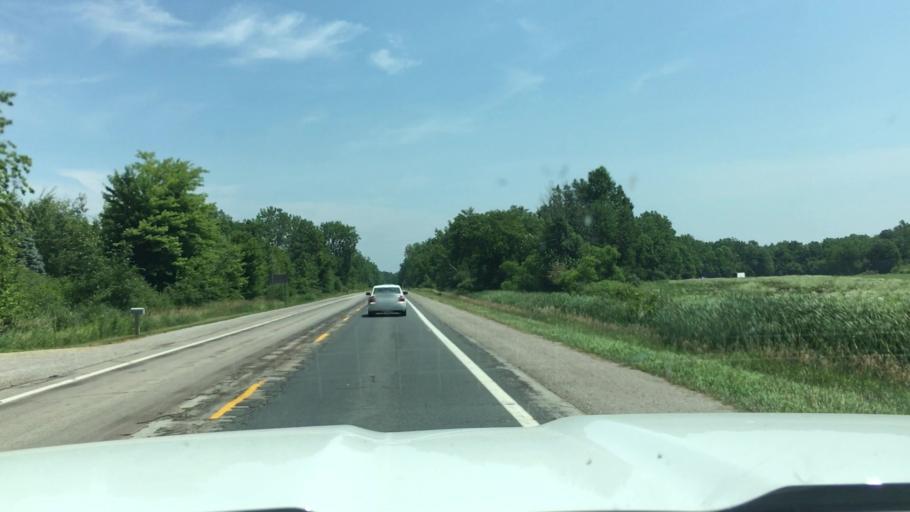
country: US
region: Michigan
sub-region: Clinton County
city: Ovid
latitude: 43.1820
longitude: -84.3449
